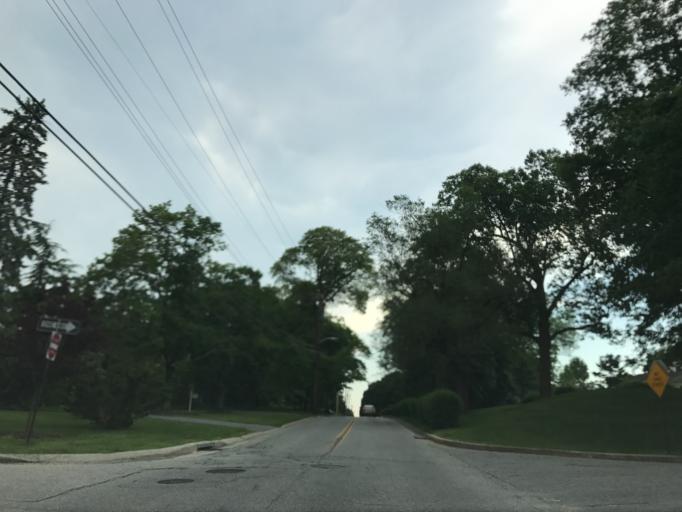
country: US
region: Maryland
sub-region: Baltimore County
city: Towson
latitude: 39.3686
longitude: -76.6213
